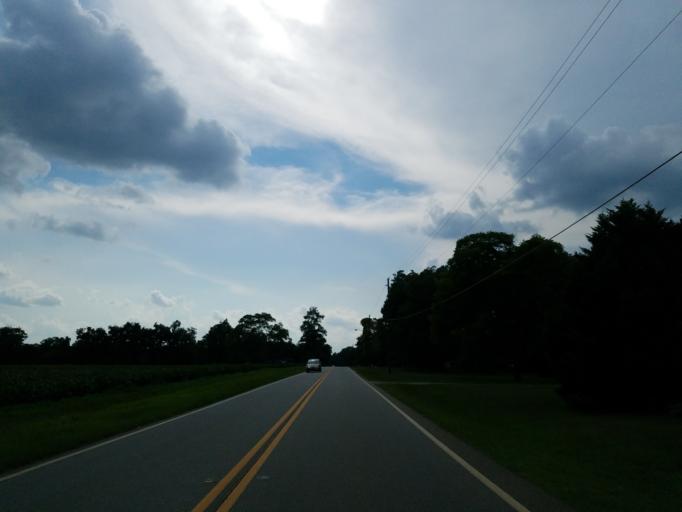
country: US
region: Georgia
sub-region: Dooly County
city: Unadilla
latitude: 32.2604
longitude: -83.7234
